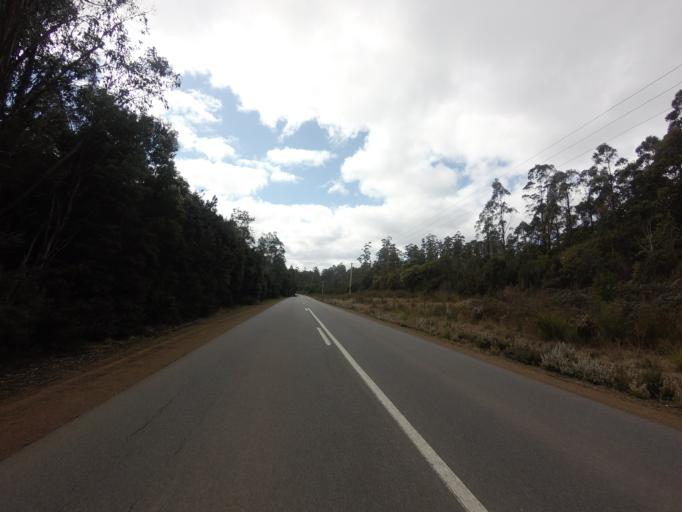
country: AU
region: Tasmania
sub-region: Huon Valley
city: Geeveston
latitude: -43.3686
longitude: 146.9582
